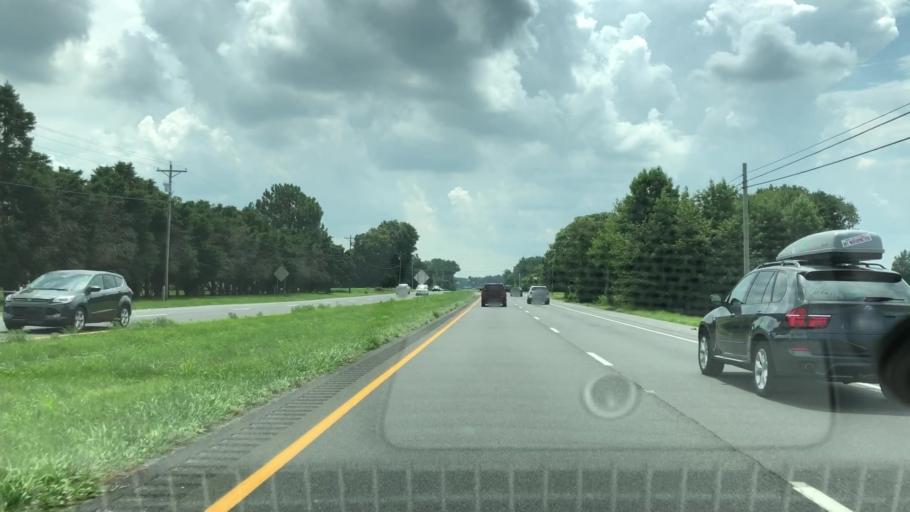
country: US
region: Delaware
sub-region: Sussex County
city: Bridgeville
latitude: 38.7980
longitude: -75.5881
